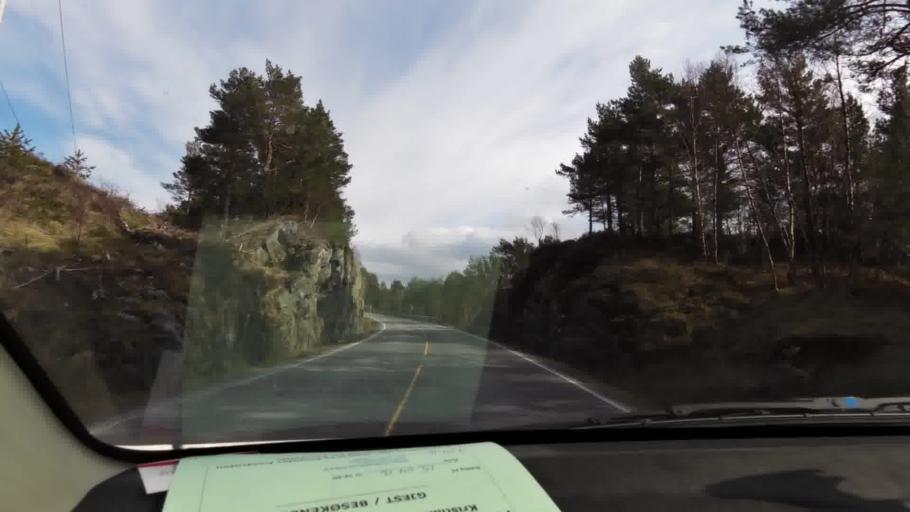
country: NO
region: More og Romsdal
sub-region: Kristiansund
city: Rensvik
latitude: 63.1073
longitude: 7.8240
